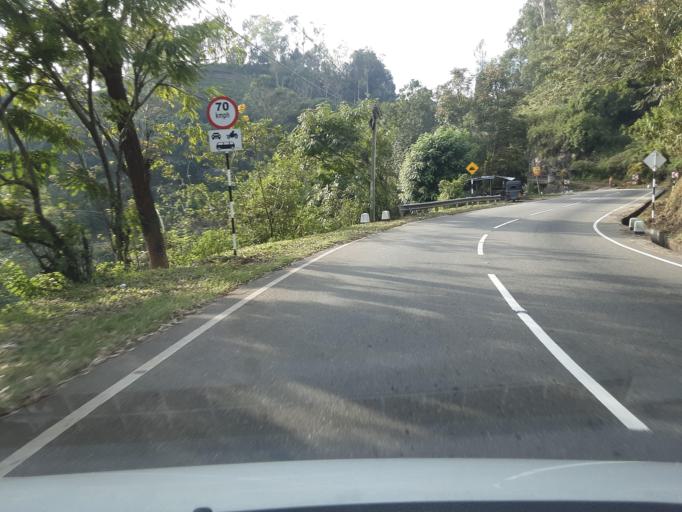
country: LK
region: Uva
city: Badulla
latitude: 6.9369
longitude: 80.9963
